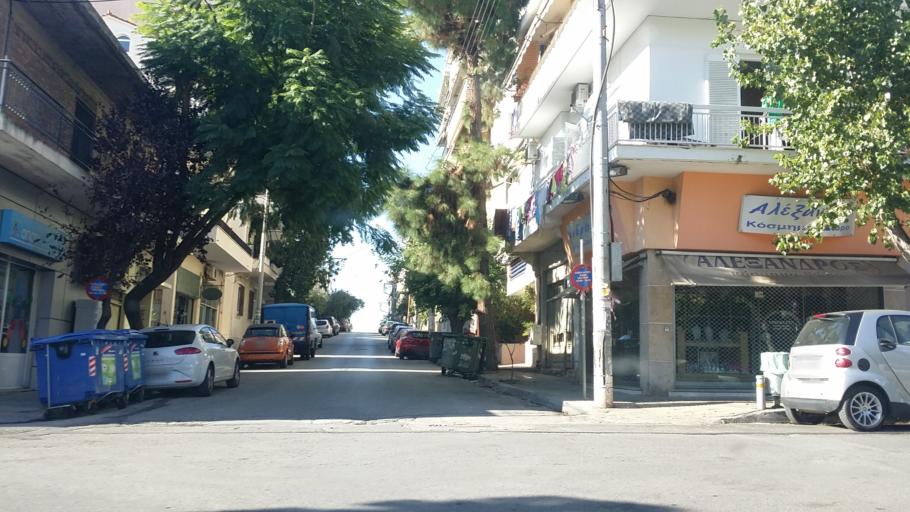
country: GR
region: Attica
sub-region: Nomarchia Athinas
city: Nea Ionia
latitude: 38.0385
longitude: 23.7672
